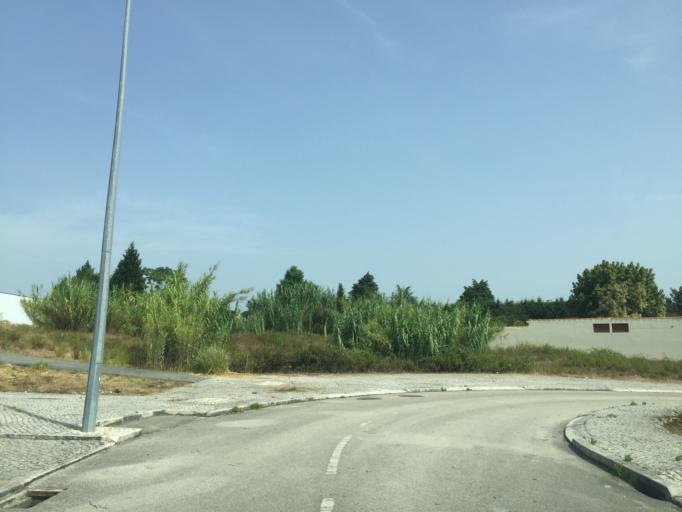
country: PT
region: Leiria
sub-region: Batalha
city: Batalha
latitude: 39.6608
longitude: -8.8301
